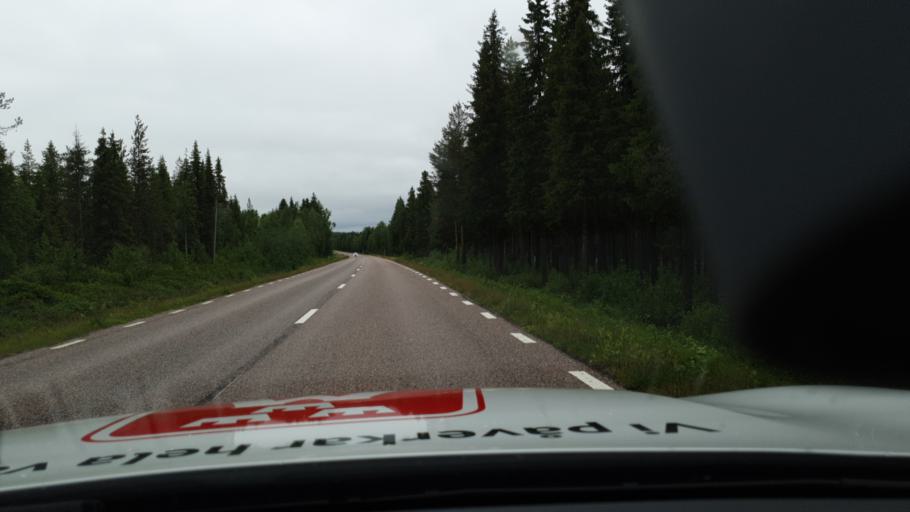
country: FI
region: Lapland
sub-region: Tunturi-Lappi
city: Kolari
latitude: 67.0585
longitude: 23.6748
